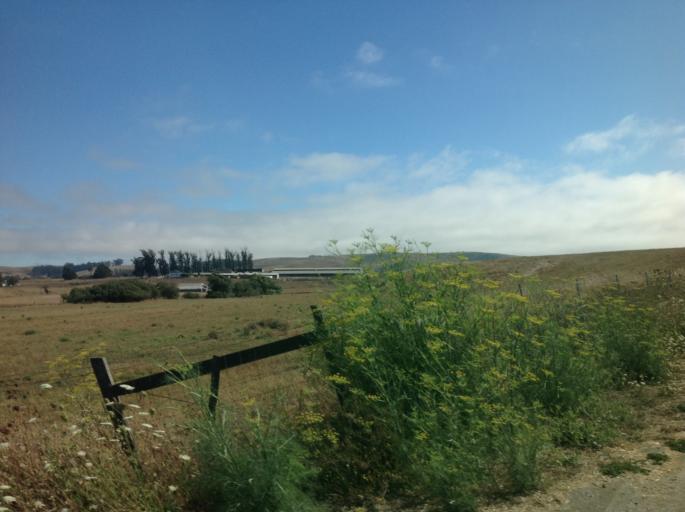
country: US
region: California
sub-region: Sonoma County
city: Occidental
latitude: 38.3250
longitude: -122.9306
